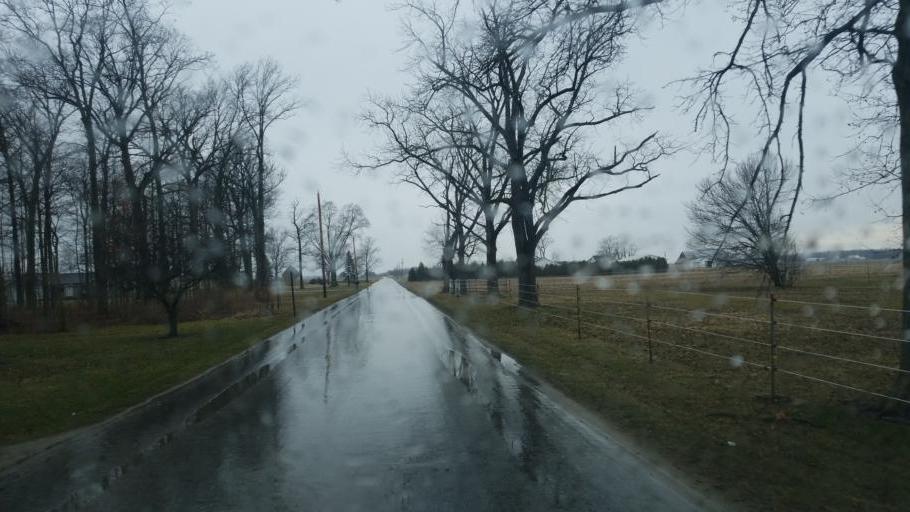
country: US
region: Indiana
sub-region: Adams County
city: Berne
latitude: 40.6723
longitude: -84.9581
